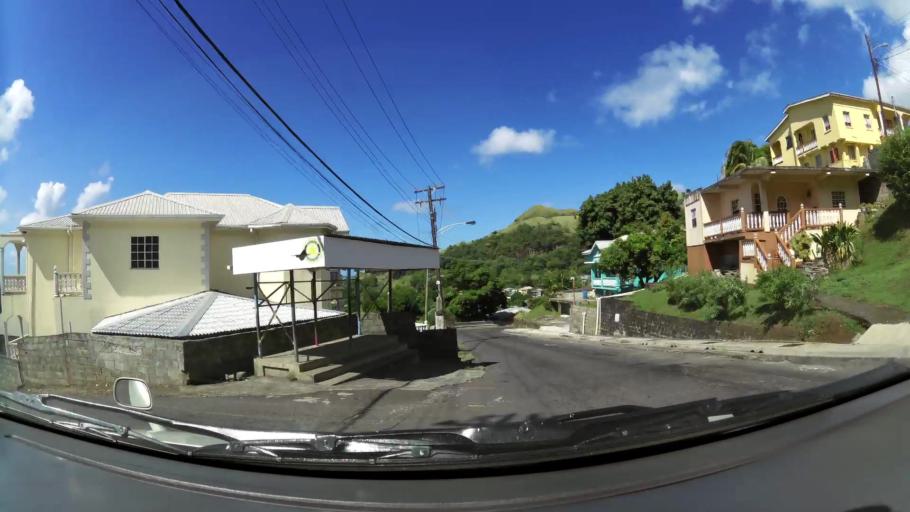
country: VC
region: Saint George
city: Kingstown Park
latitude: 13.1733
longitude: -61.2354
